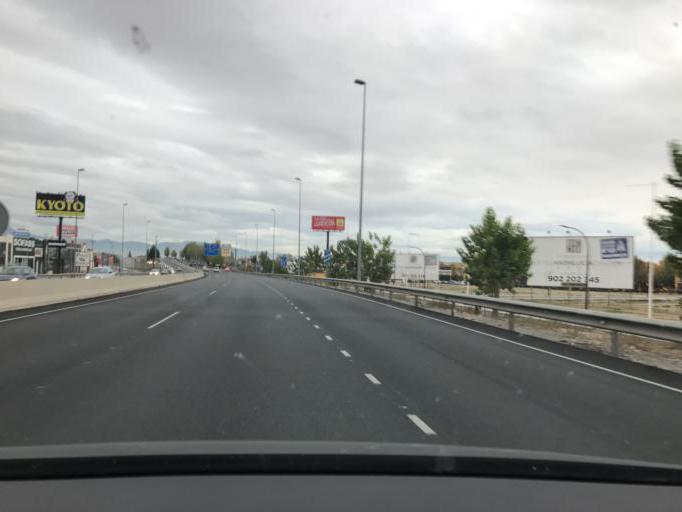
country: ES
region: Andalusia
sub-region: Provincia de Granada
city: Maracena
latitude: 37.2153
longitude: -3.6245
